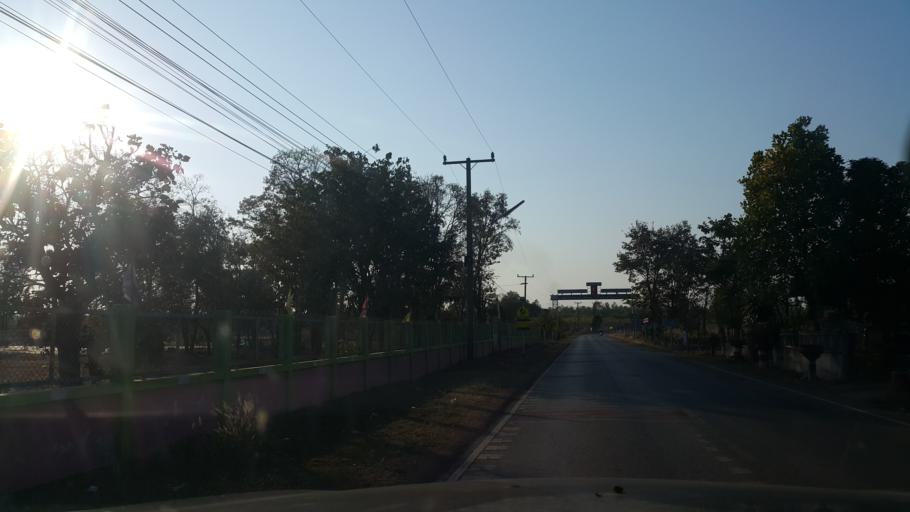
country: TH
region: Changwat Udon Thani
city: Ban Na Muang
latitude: 17.3037
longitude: 102.9447
